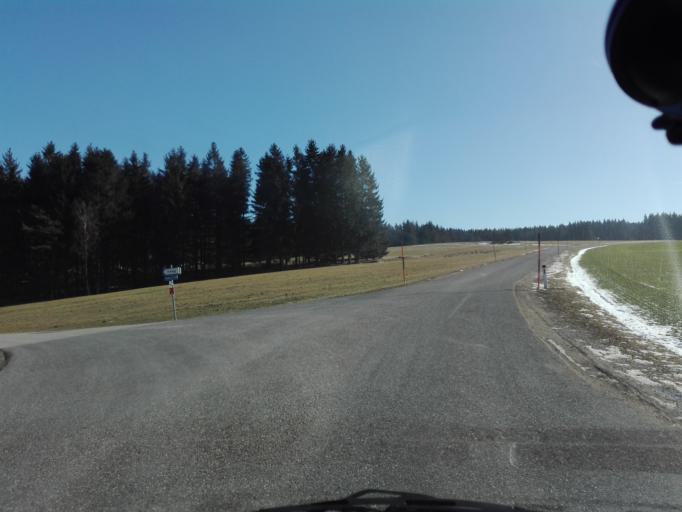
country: AT
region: Upper Austria
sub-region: Politischer Bezirk Urfahr-Umgebung
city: Sonnberg im Muehlkreis
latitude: 48.4575
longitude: 14.3015
